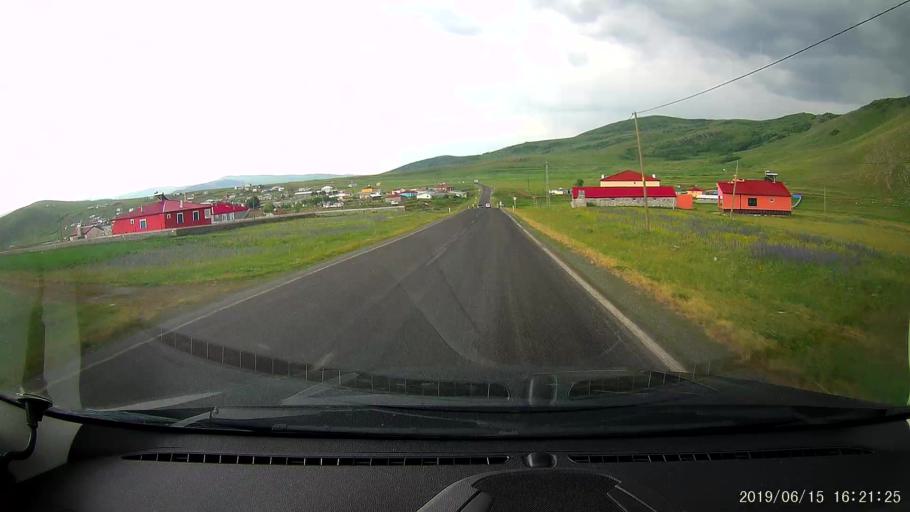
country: TR
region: Ardahan
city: Hanak
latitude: 41.1992
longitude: 42.8459
